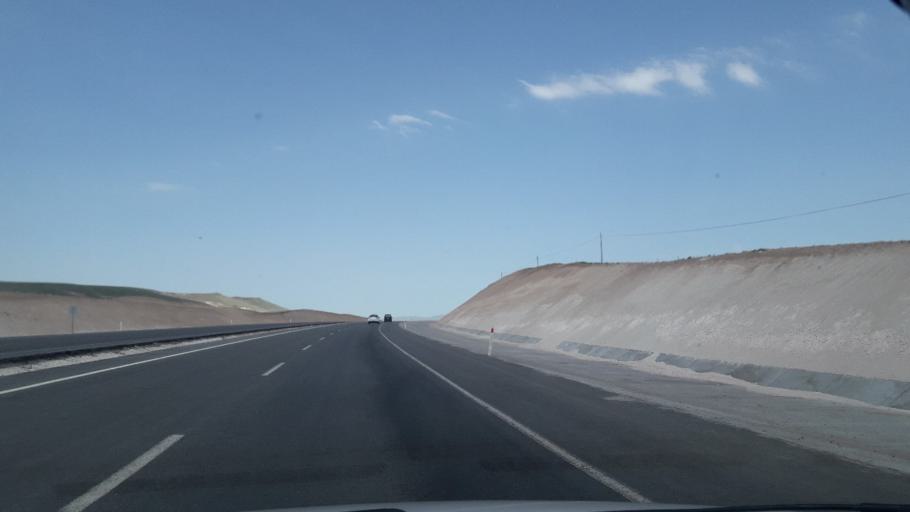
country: TR
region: Sivas
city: Deliktas
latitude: 39.2031
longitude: 37.2241
